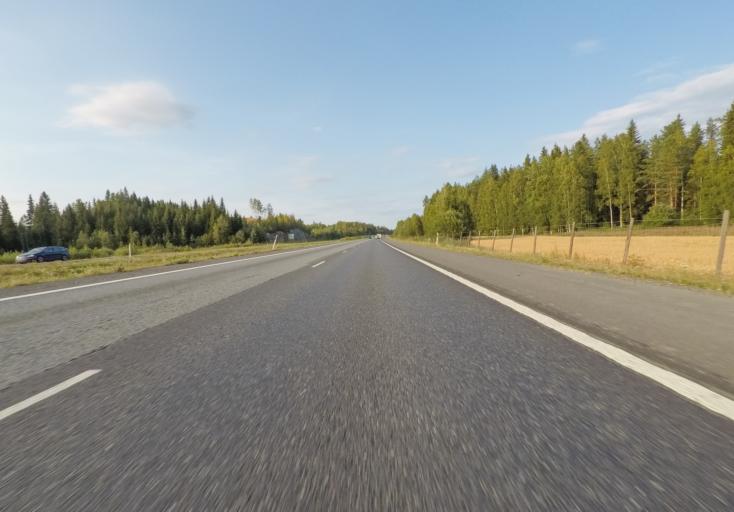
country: FI
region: Paijanne Tavastia
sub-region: Lahti
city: Heinola
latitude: 61.1289
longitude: 25.9408
